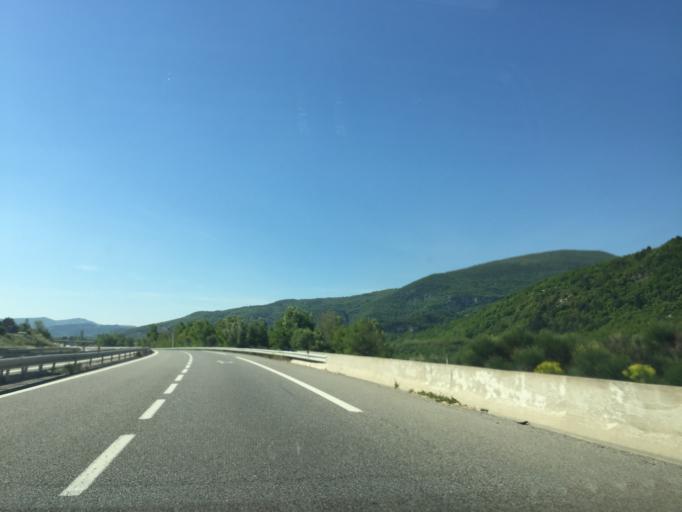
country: FR
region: Provence-Alpes-Cote d'Azur
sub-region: Departement des Alpes-de-Haute-Provence
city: Sisteron
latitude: 44.1748
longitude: 5.9537
